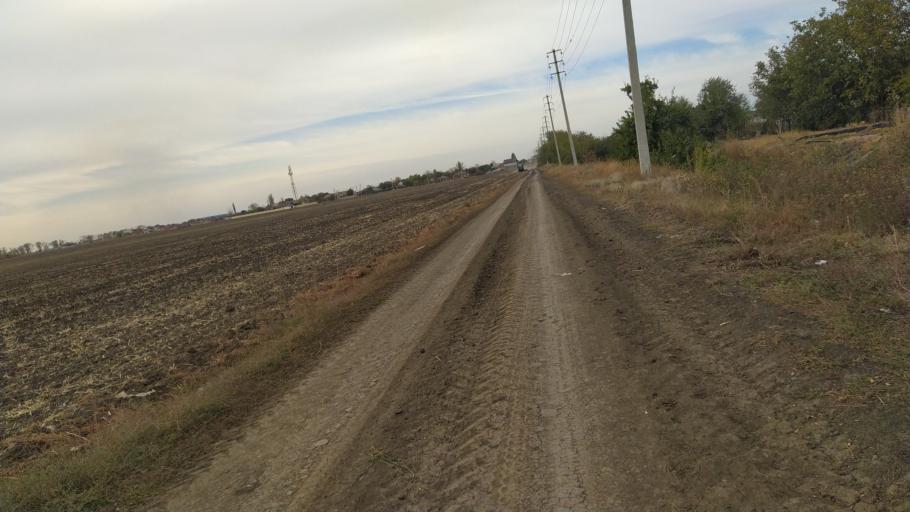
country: RU
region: Rostov
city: Bataysk
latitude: 47.1090
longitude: 39.6843
